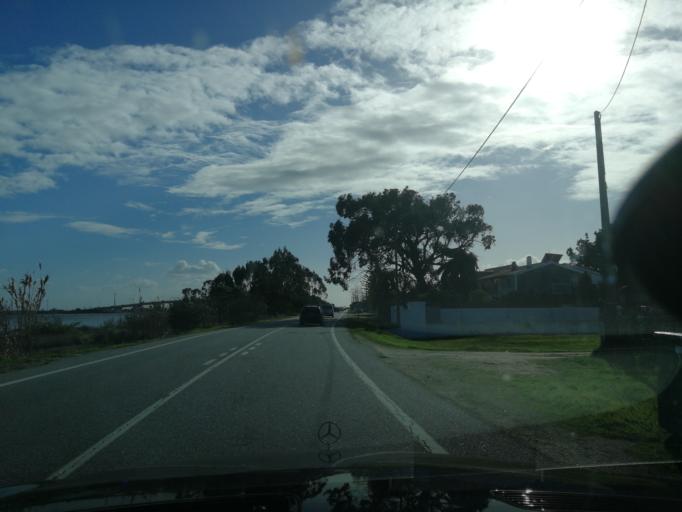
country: PT
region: Aveiro
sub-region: Estarreja
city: Pardilho
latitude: 40.7958
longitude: -8.6735
